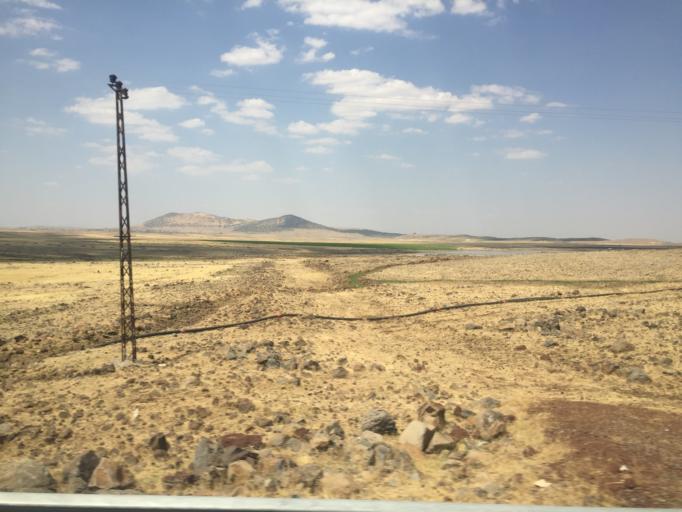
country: TR
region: Sanliurfa
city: Karacadag
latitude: 37.8509
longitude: 39.7187
